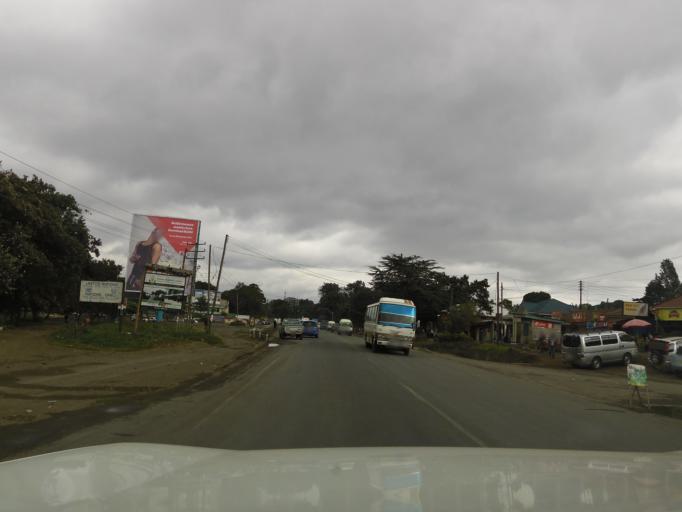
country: TZ
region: Arusha
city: Arusha
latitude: -3.3621
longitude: 36.6975
